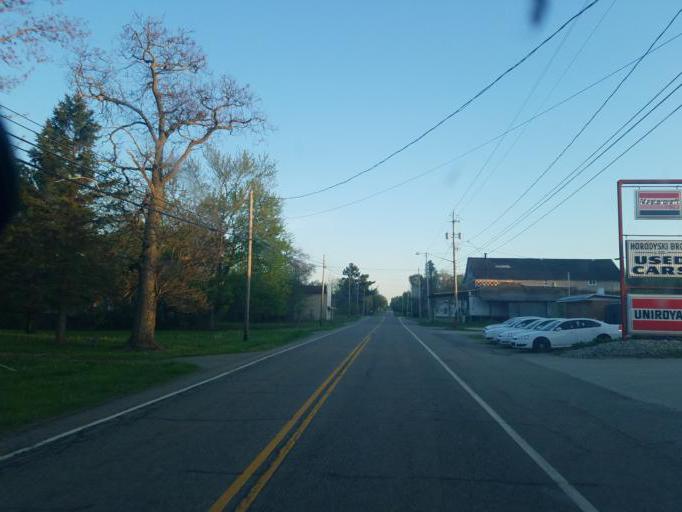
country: US
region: Ohio
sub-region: Trumbull County
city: Brookfield Center
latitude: 41.3589
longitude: -80.5692
